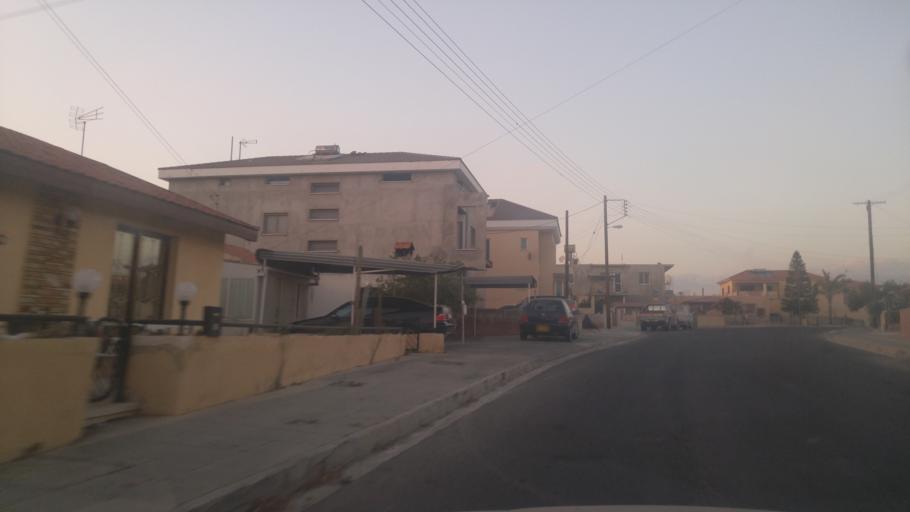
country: CY
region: Larnaka
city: Kolossi
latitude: 34.6599
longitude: 32.9564
